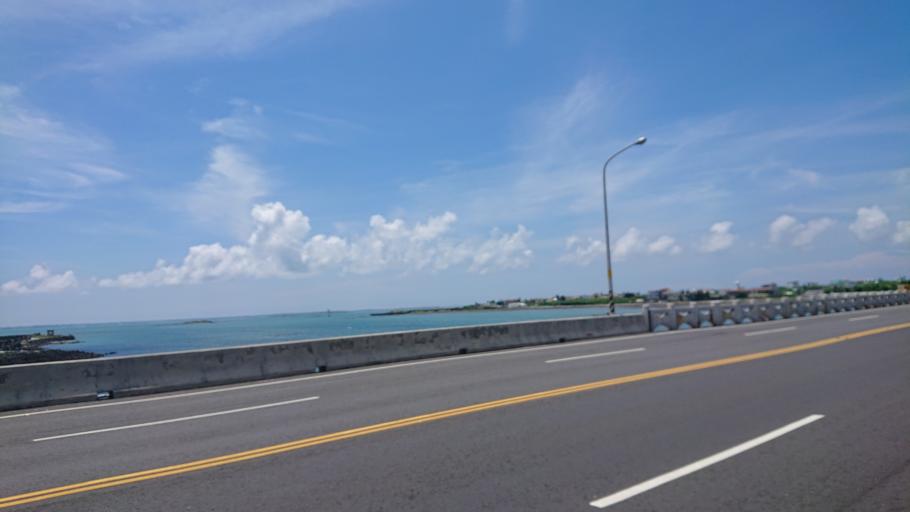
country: TW
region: Taiwan
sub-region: Penghu
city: Ma-kung
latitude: 23.6056
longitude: 119.6125
